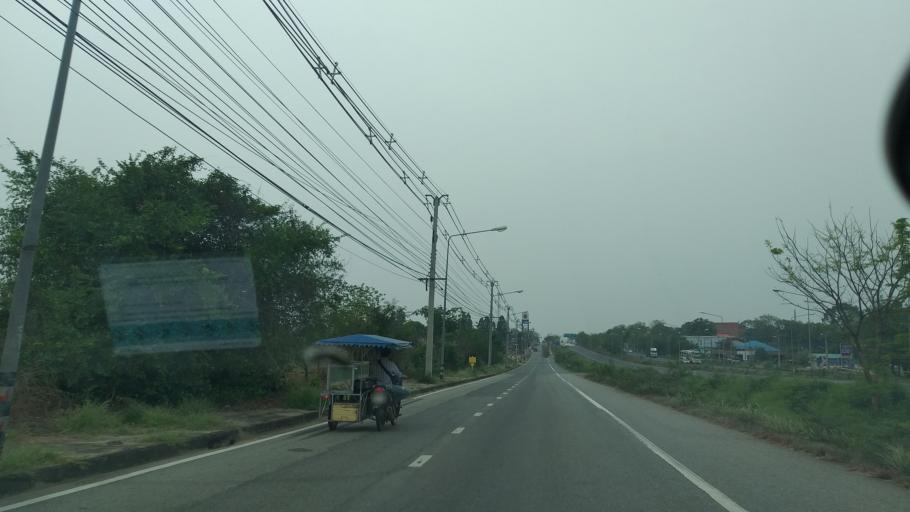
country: TH
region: Chon Buri
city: Ko Chan
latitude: 13.4792
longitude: 101.2816
